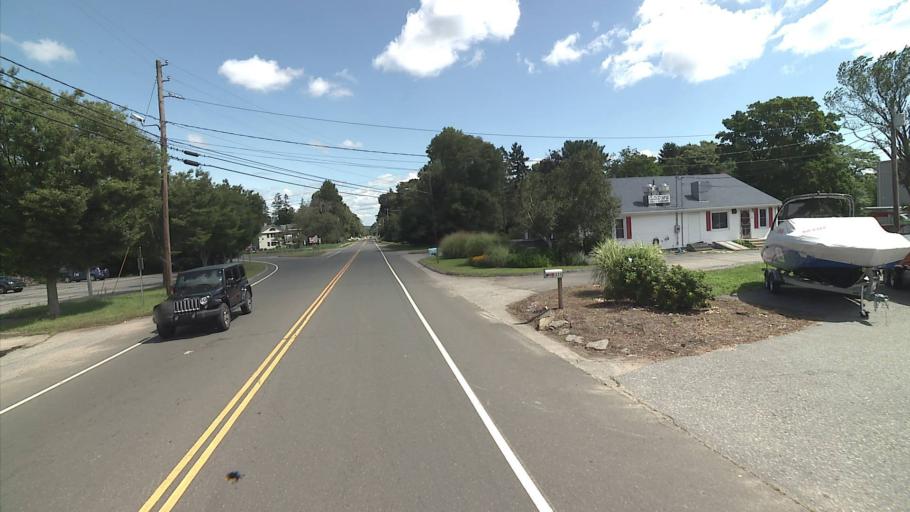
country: US
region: Connecticut
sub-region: Middlesex County
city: Old Saybrook Center
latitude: 41.3087
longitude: -72.3678
